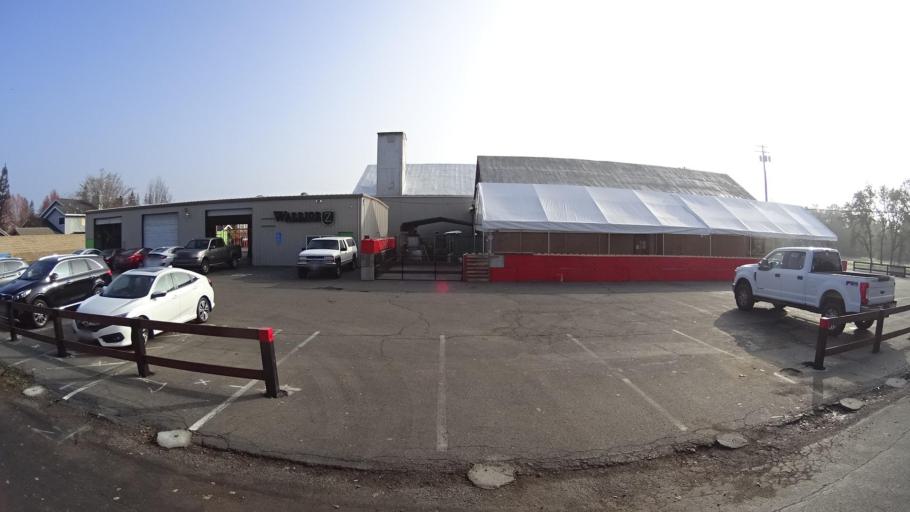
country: US
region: California
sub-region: Sacramento County
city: Elk Grove
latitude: 38.4095
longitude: -121.3564
